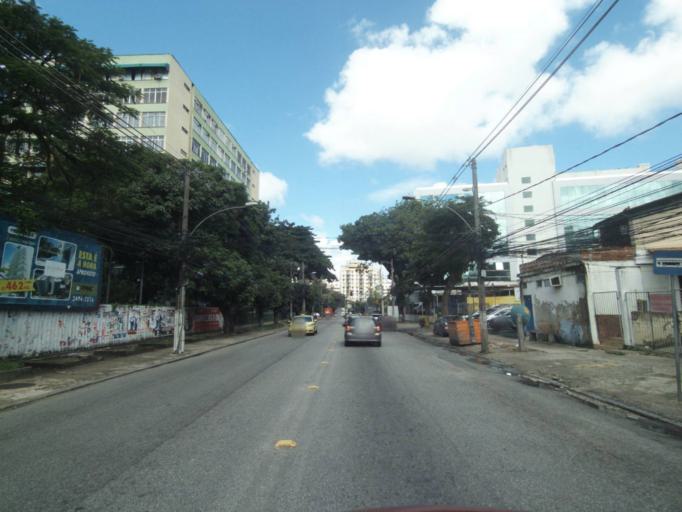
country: BR
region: Rio de Janeiro
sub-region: Sao Joao De Meriti
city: Sao Joao de Meriti
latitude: -22.9323
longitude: -43.3530
